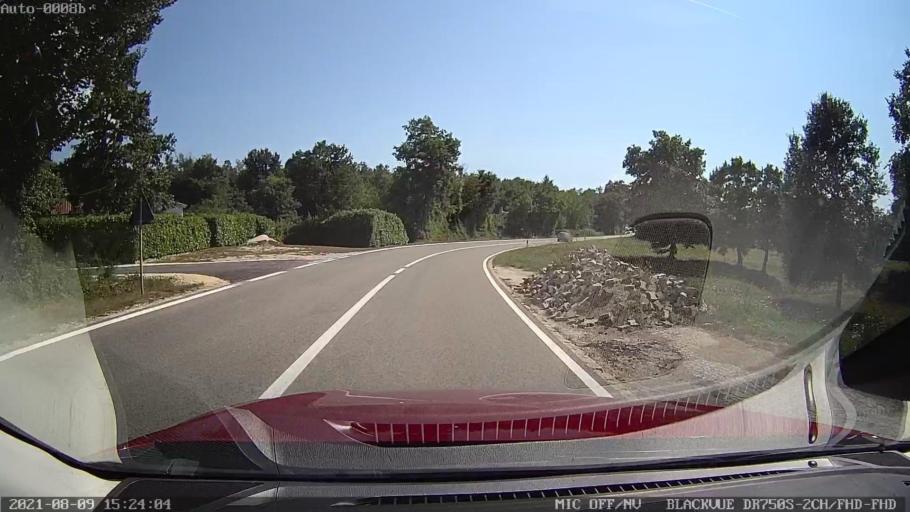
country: HR
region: Istarska
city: Pazin
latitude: 45.1784
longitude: 13.9047
